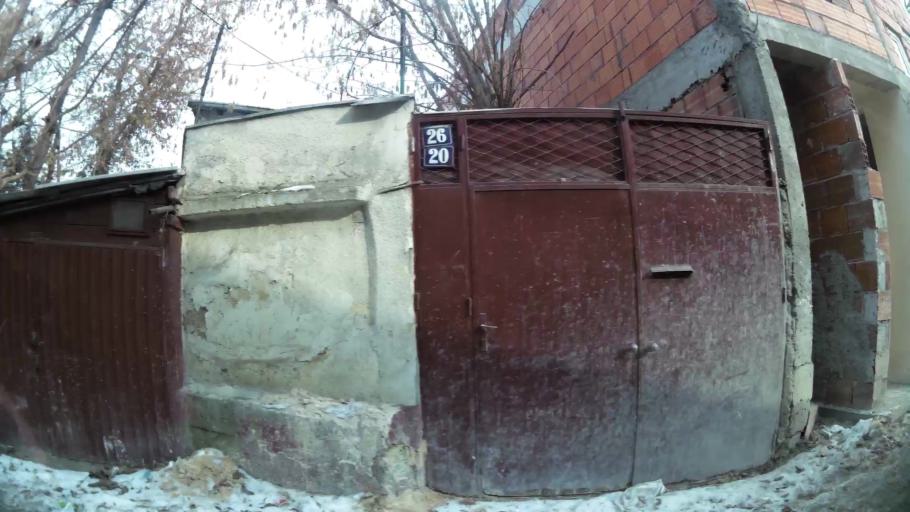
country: MK
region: Cair
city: Cair
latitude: 42.0116
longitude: 21.4461
